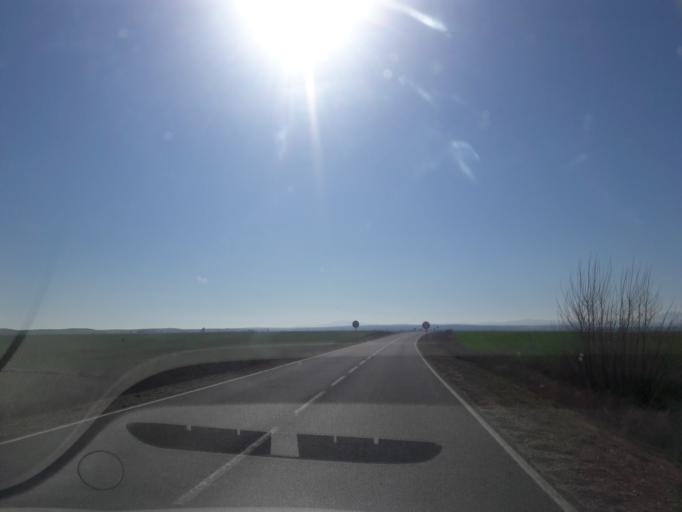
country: ES
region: Castille and Leon
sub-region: Provincia de Salamanca
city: Santiago de la Puebla
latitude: 40.8130
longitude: -5.2553
